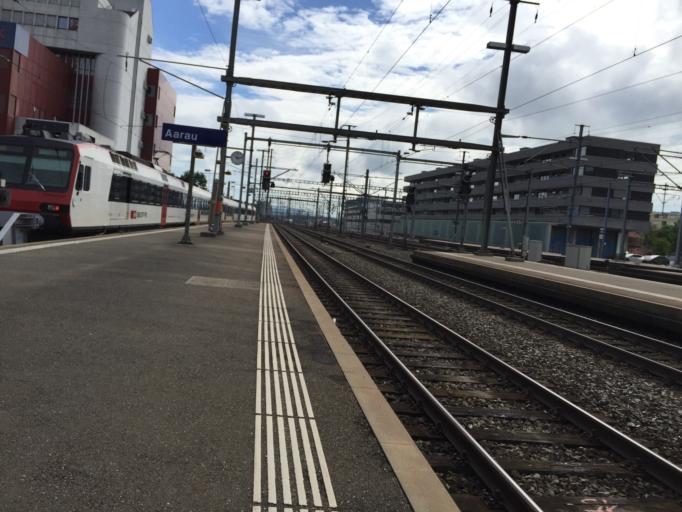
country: CH
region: Aargau
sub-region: Bezirk Aarau
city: Aarau
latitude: 47.3919
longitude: 8.0537
